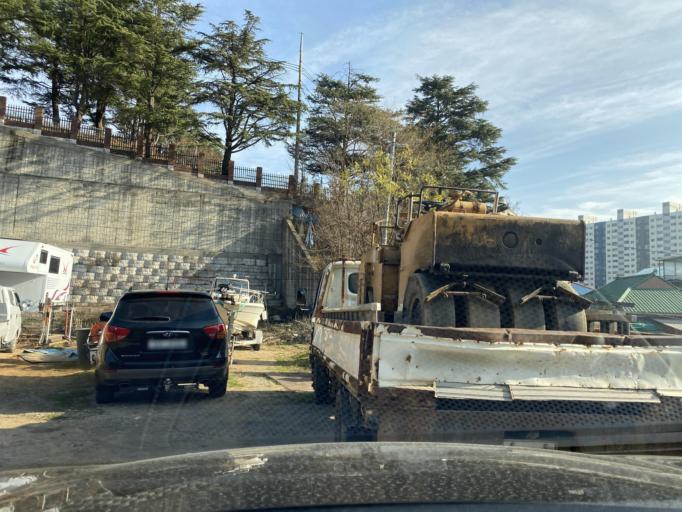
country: KR
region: Chungcheongnam-do
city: Yesan
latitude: 36.6805
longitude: 126.8361
